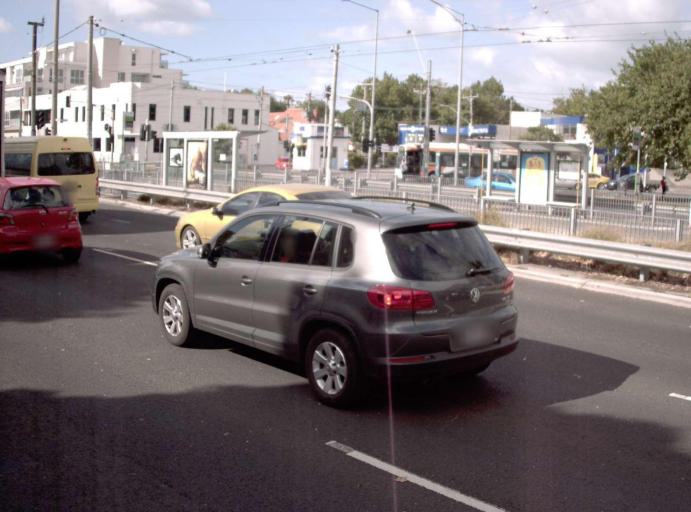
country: AU
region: Victoria
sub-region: Port Phillip
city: Saint Kilda
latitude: -37.8672
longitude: 144.9868
